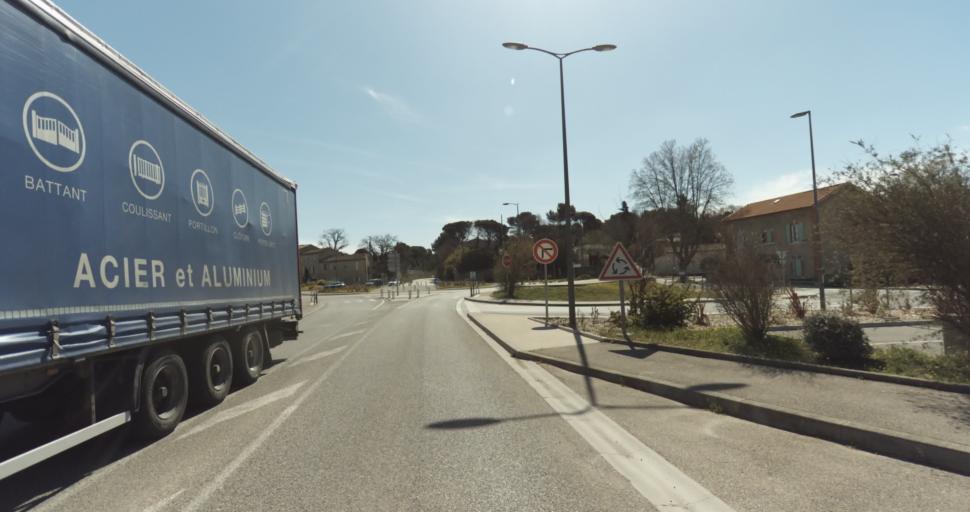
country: FR
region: Provence-Alpes-Cote d'Azur
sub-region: Departement des Bouches-du-Rhone
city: Lambesc
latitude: 43.6545
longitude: 5.2690
